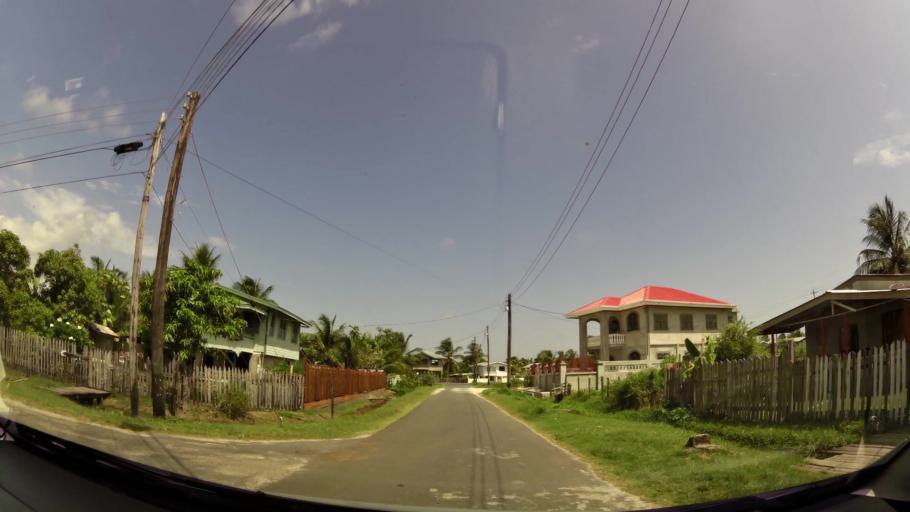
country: GY
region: Demerara-Mahaica
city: Mahaica Village
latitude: 6.7754
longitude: -58.0120
